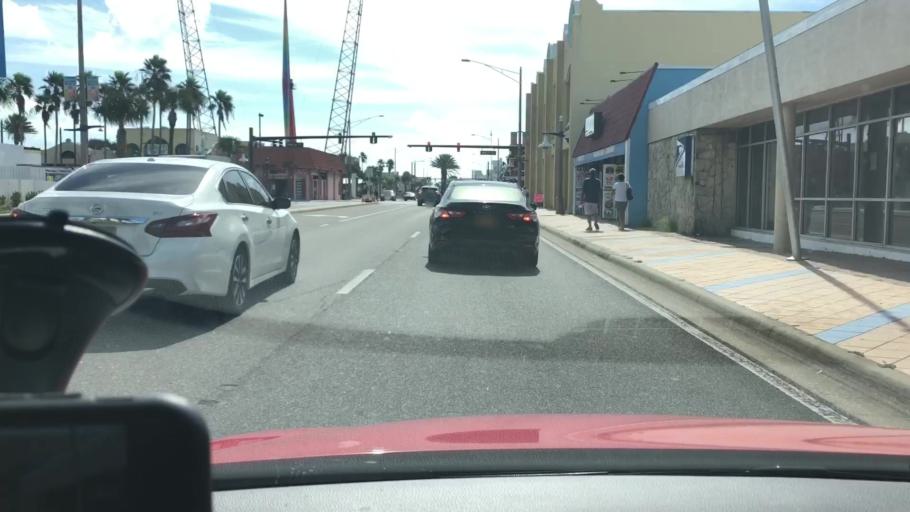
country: US
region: Florida
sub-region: Volusia County
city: Daytona Beach
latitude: 29.2274
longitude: -81.0086
